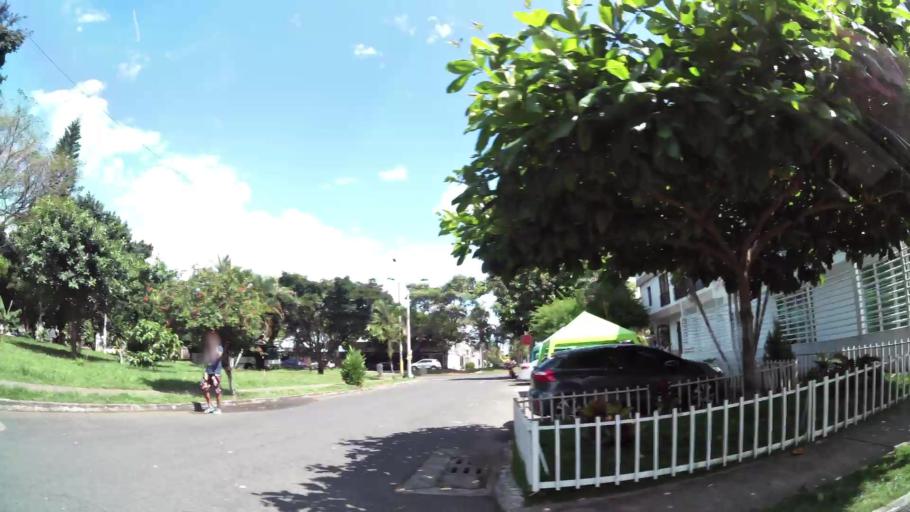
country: CO
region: Valle del Cauca
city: Cali
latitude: 3.3959
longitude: -76.5181
